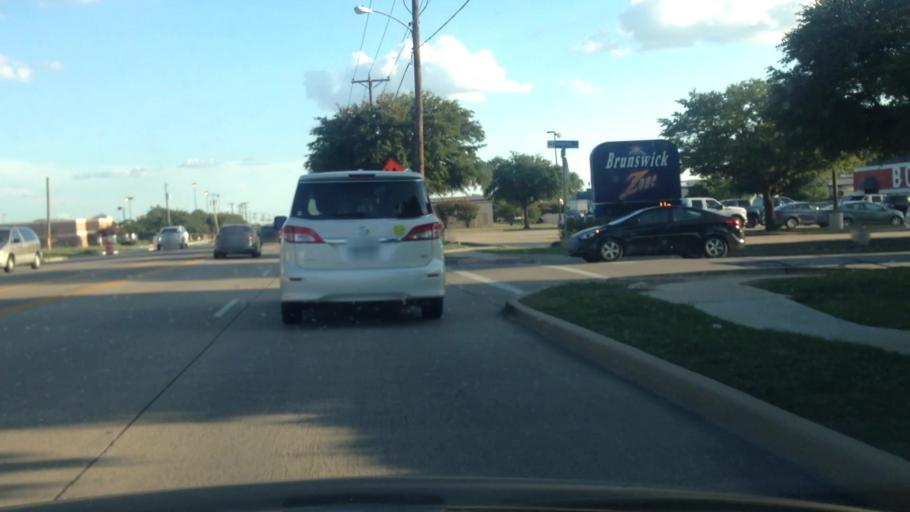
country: US
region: Texas
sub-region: Tarrant County
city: Watauga
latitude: 32.8784
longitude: -97.2380
